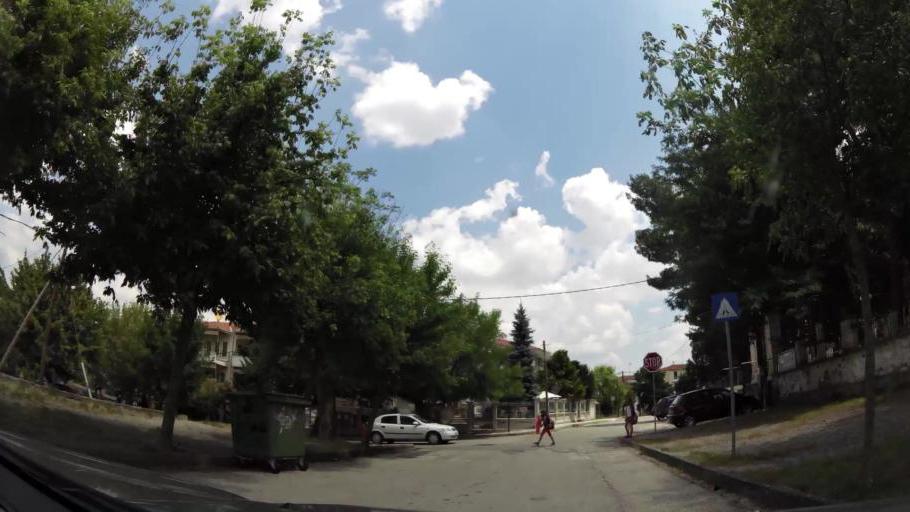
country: GR
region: West Macedonia
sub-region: Nomos Kozanis
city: Kozani
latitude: 40.2920
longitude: 21.7867
